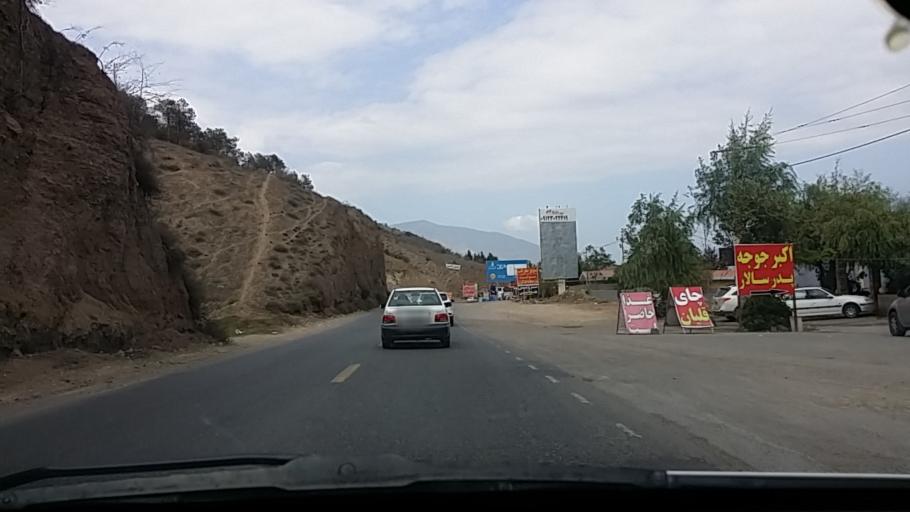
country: IR
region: Mazandaran
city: Chalus
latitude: 36.4338
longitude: 51.2882
